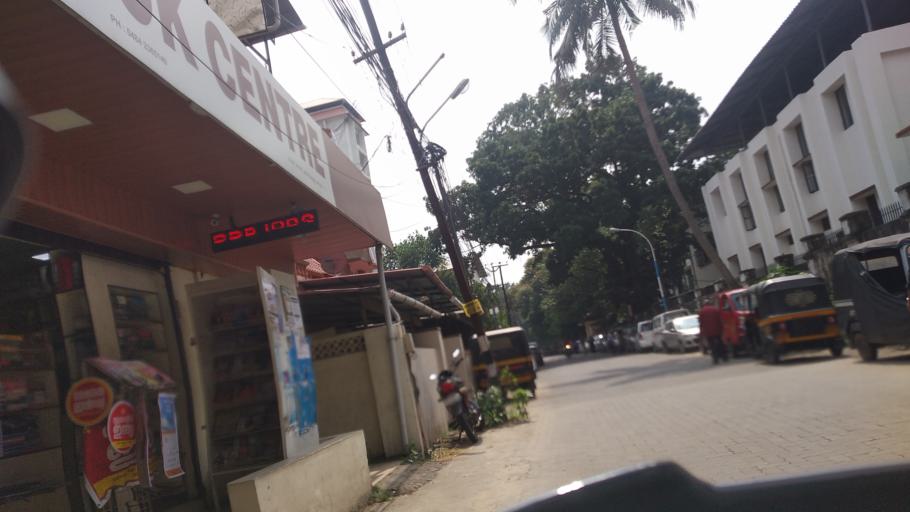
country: IN
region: Kerala
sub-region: Ernakulam
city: Cochin
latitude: 9.9717
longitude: 76.2823
